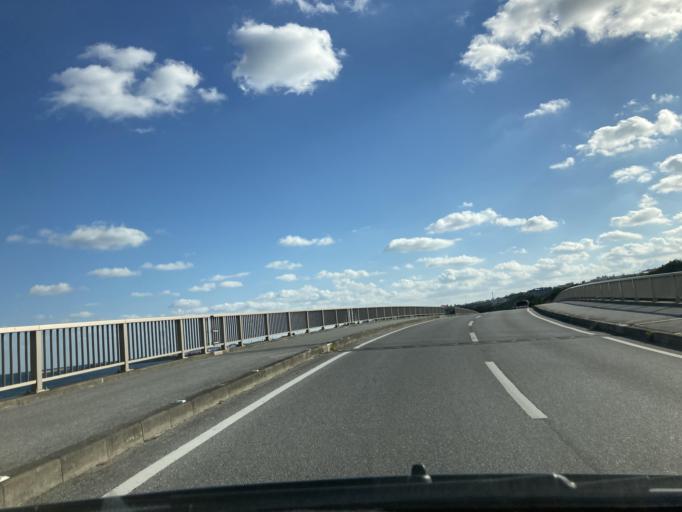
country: JP
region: Okinawa
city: Katsuren-haebaru
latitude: 26.3170
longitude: 127.9183
